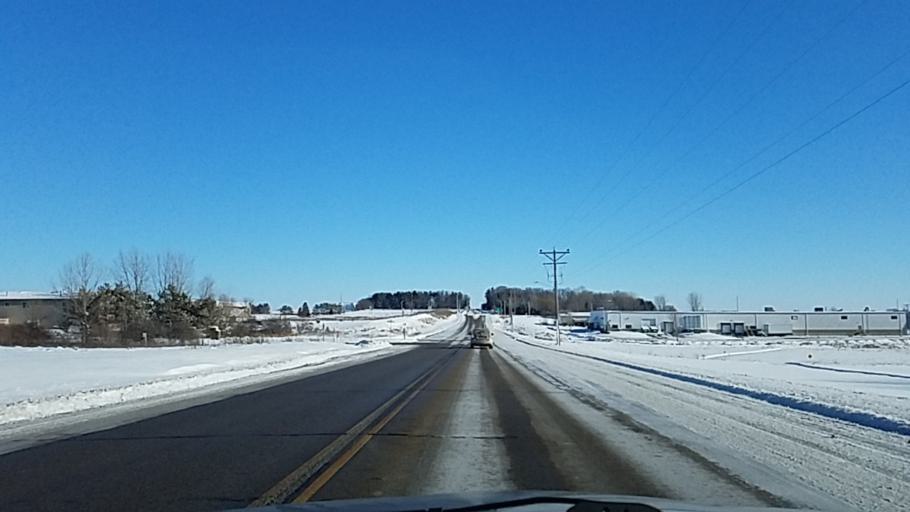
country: US
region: Wisconsin
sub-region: Saint Croix County
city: Roberts
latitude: 44.9925
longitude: -92.5457
